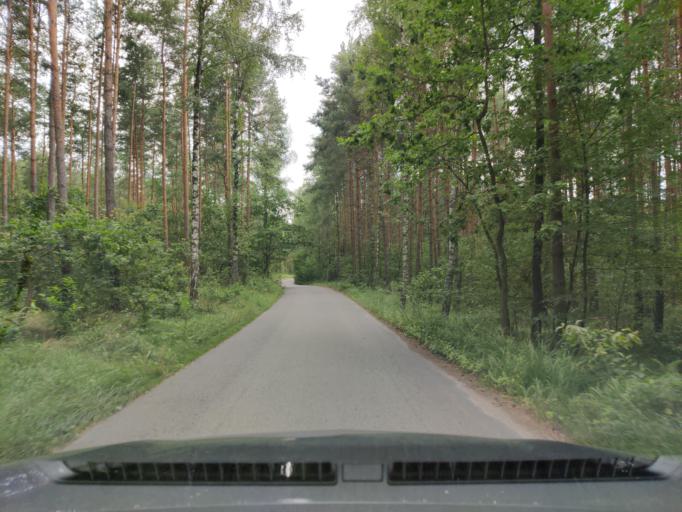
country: PL
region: Masovian Voivodeship
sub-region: Powiat pultuski
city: Pultusk
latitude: 52.7406
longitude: 21.1406
